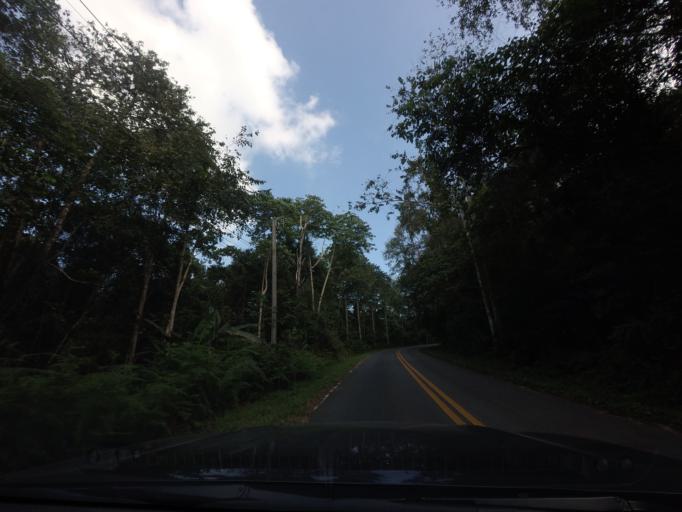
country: TH
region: Phitsanulok
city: Nakhon Thai
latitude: 16.9891
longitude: 101.0181
